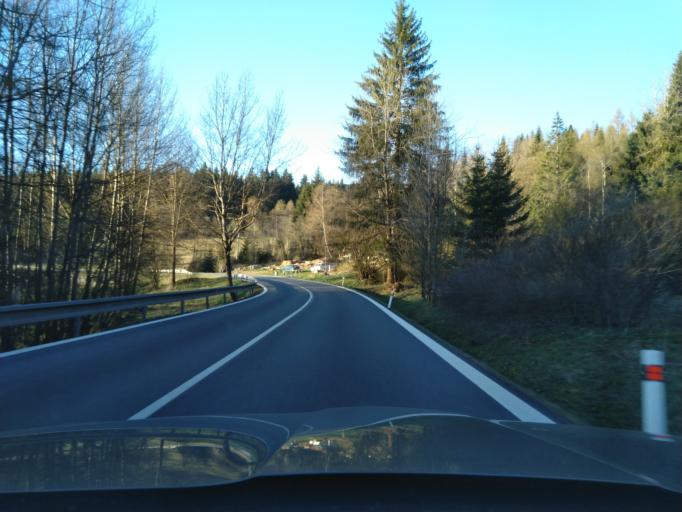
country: CZ
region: Jihocesky
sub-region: Okres Prachatice
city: Vimperk
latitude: 49.0036
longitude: 13.7650
